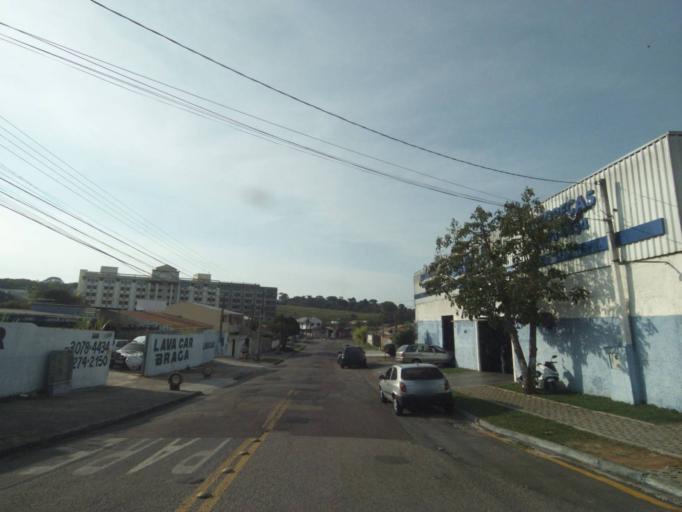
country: BR
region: Parana
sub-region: Curitiba
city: Curitiba
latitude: -25.4583
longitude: -49.3148
